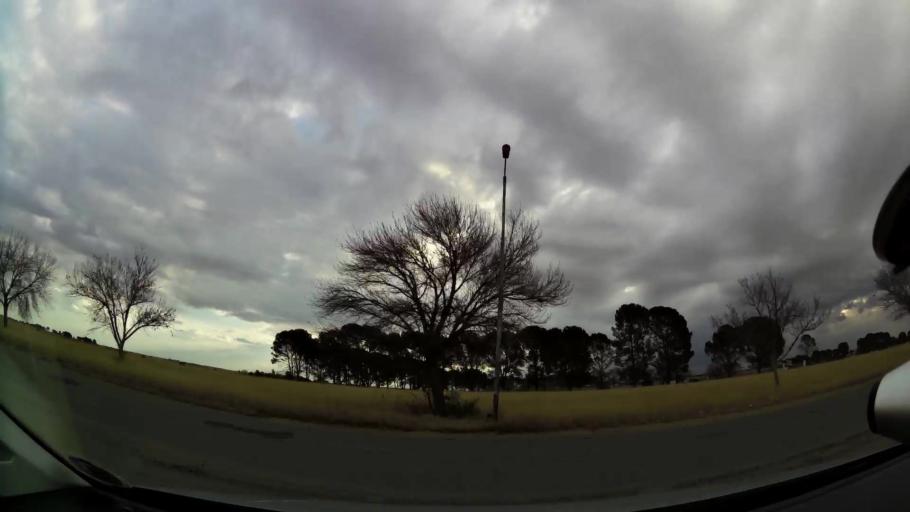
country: ZA
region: Orange Free State
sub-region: Lejweleputswa District Municipality
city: Welkom
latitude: -27.9781
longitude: 26.6961
